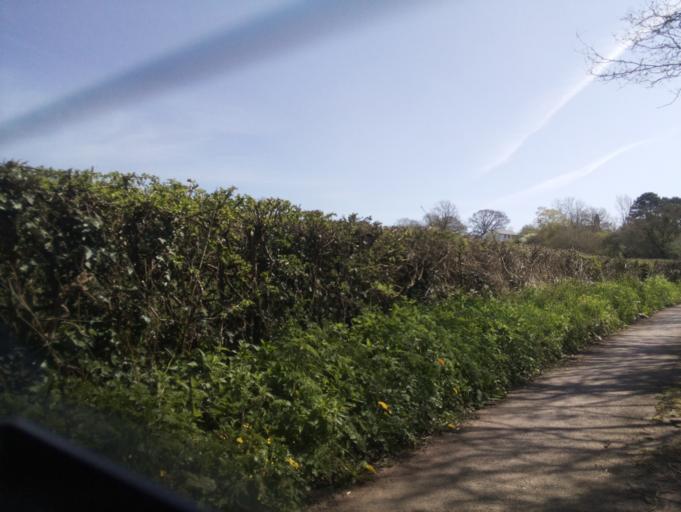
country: GB
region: Wales
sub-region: Monmouthshire
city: Llangwm
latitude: 51.7128
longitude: -2.8506
